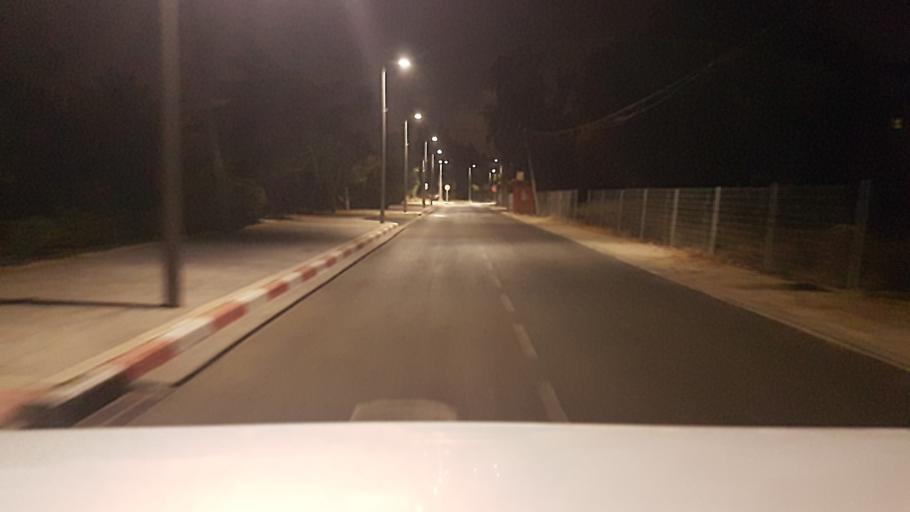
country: IL
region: Central District
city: Nehalim
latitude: 32.0780
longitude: 34.9241
